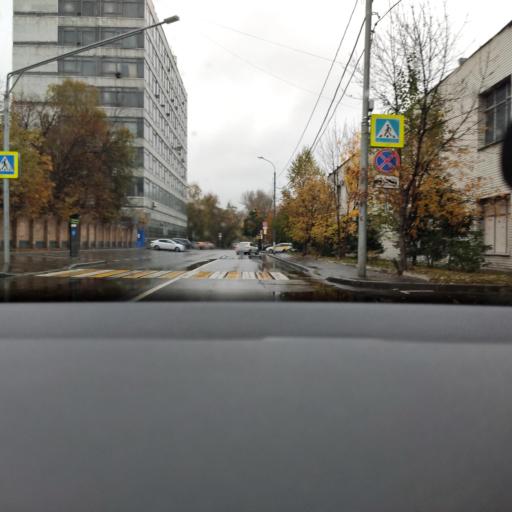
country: RU
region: Moscow
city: Ryazanskiy
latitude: 55.7512
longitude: 37.7695
